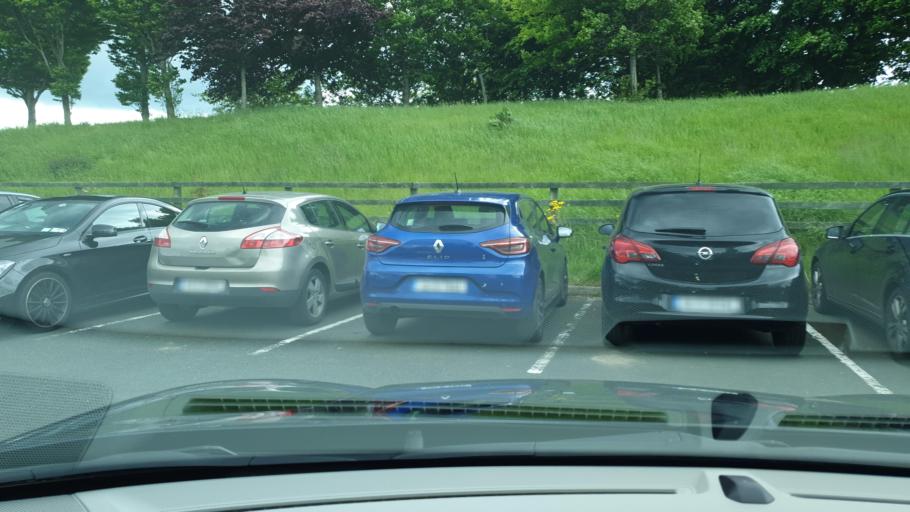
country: IE
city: Kilquade
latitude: 53.0909
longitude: -6.0784
